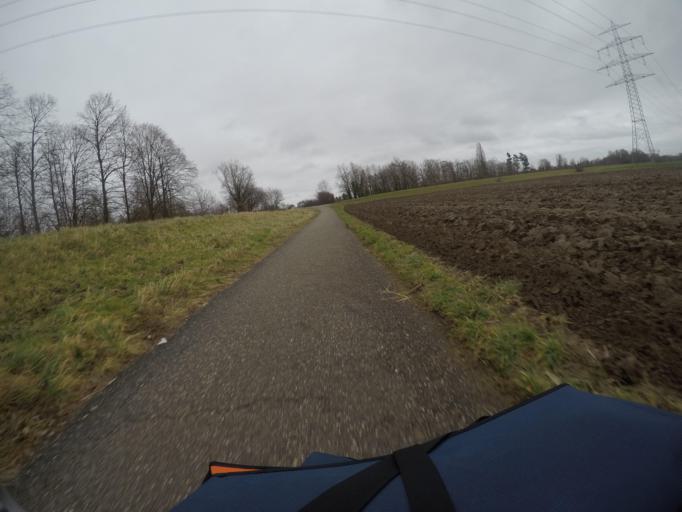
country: DE
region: Baden-Wuerttemberg
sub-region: Karlsruhe Region
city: Philippsburg
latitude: 49.2417
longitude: 8.4418
